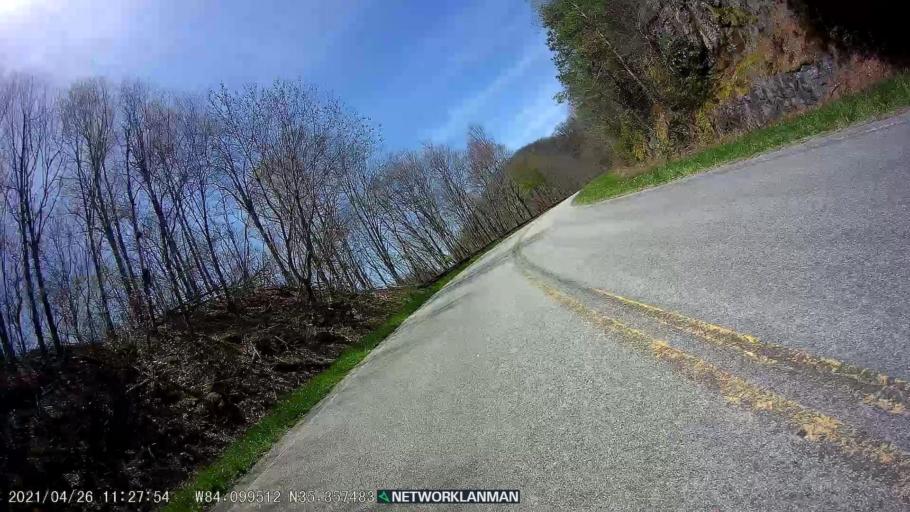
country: US
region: Tennessee
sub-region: Monroe County
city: Vonore
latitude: 35.3573
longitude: -84.0993
